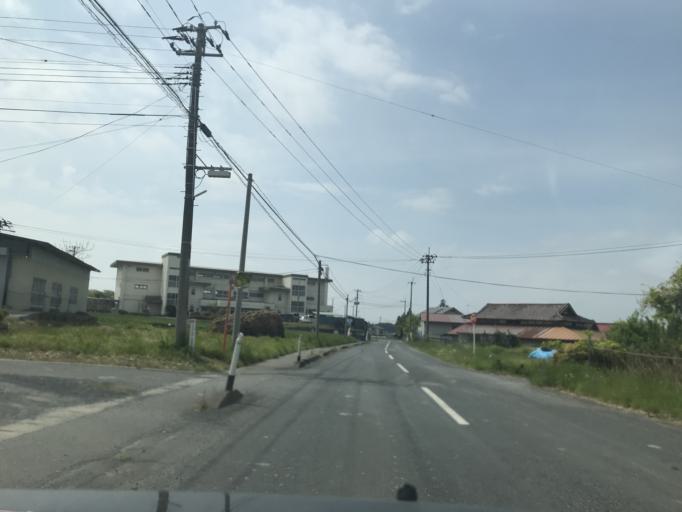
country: JP
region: Iwate
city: Ichinoseki
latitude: 38.8280
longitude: 141.2022
